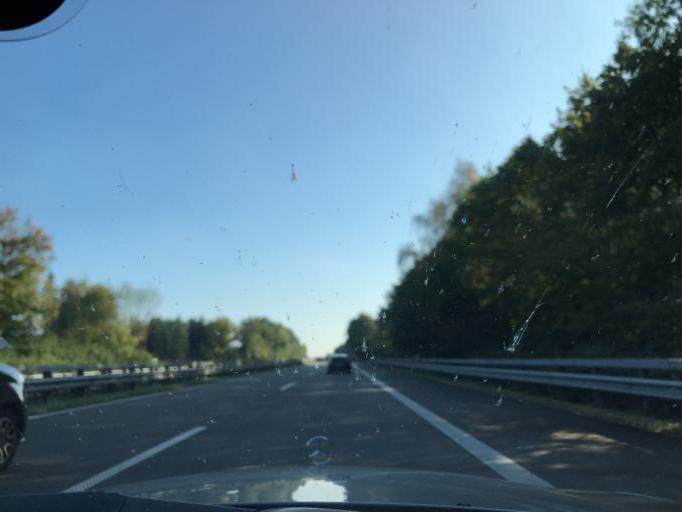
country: DE
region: Lower Saxony
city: Bad Zwischenahn
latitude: 53.2286
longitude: 8.0353
